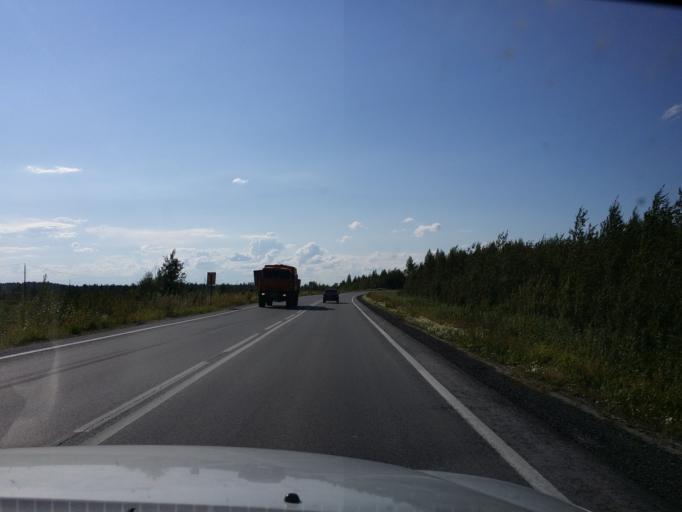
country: RU
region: Khanty-Mansiyskiy Avtonomnyy Okrug
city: Lokosovo
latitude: 61.3949
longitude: 74.8697
